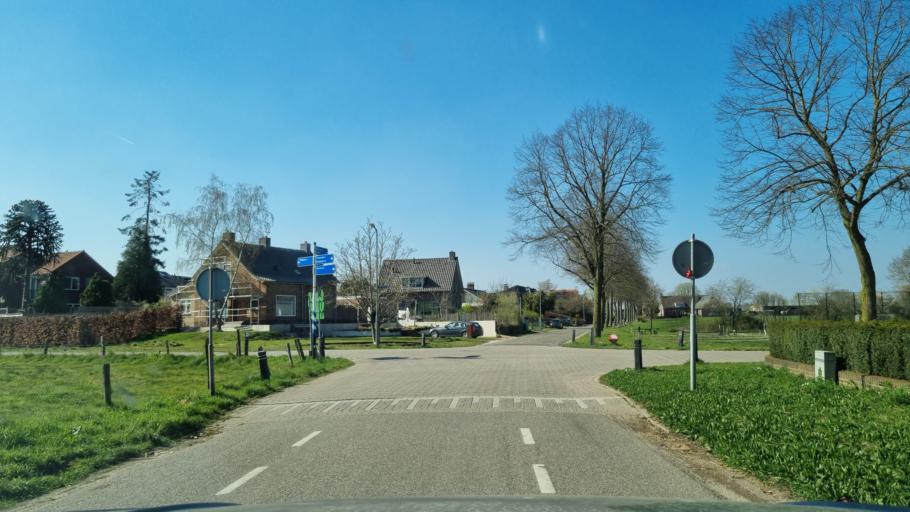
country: NL
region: North Brabant
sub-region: Gemeente Cuijk
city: Cuijk
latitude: 51.7293
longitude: 5.9128
